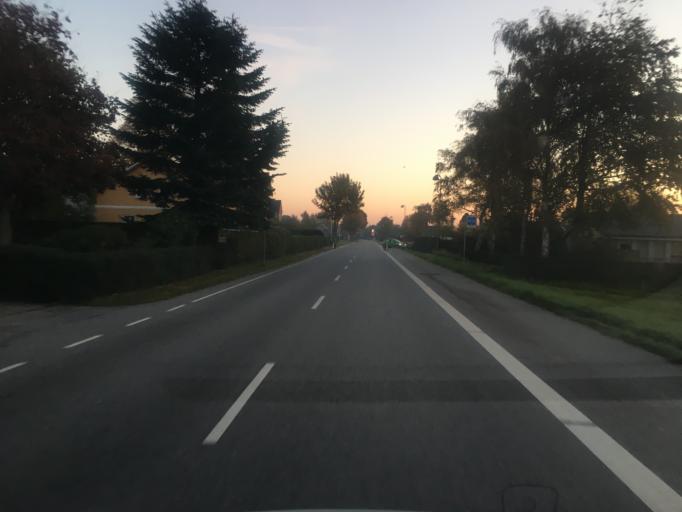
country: DE
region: Schleswig-Holstein
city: Bramstedtlund
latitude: 54.9373
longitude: 9.0792
